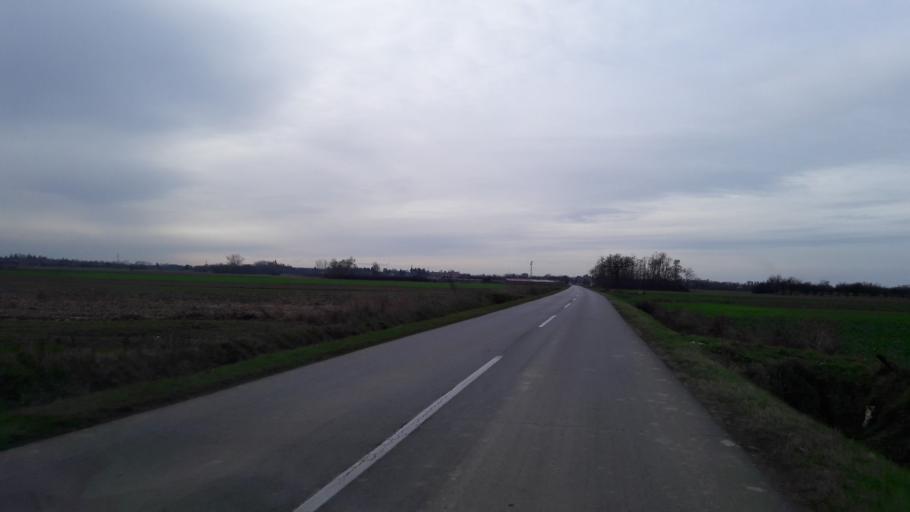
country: HR
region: Osjecko-Baranjska
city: Semeljci
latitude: 45.3728
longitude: 18.5528
